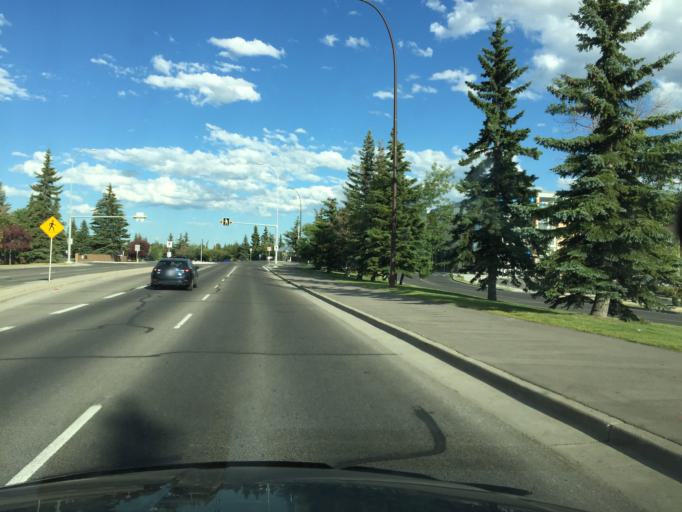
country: CA
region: Alberta
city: Calgary
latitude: 50.9545
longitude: -114.0672
